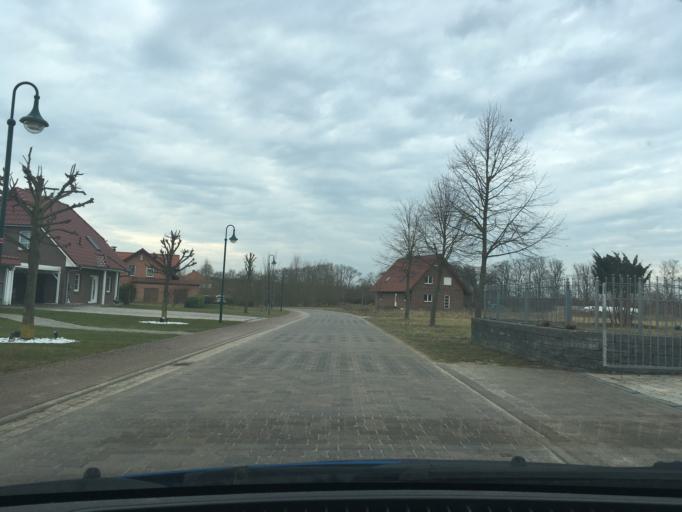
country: DE
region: Mecklenburg-Vorpommern
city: Zarrentin
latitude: 53.5592
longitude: 10.9171
